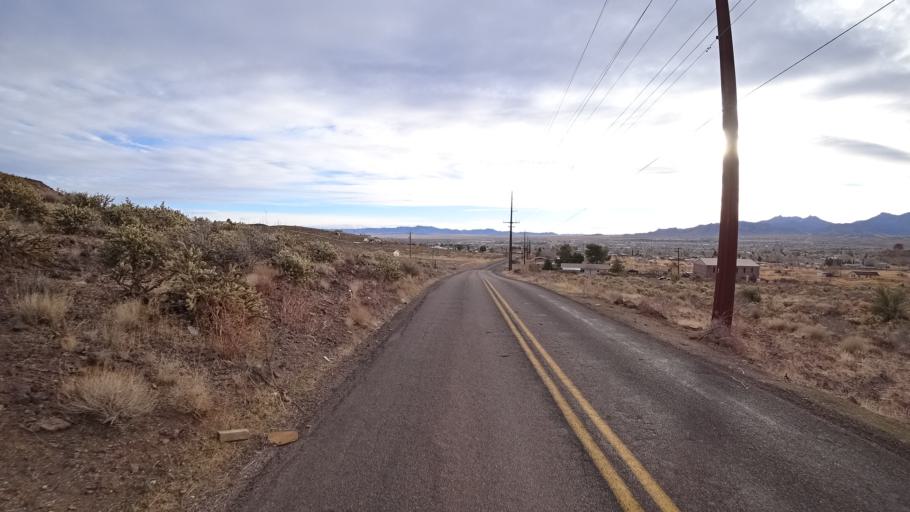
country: US
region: Arizona
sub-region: Mohave County
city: Kingman
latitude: 35.2179
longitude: -114.0595
